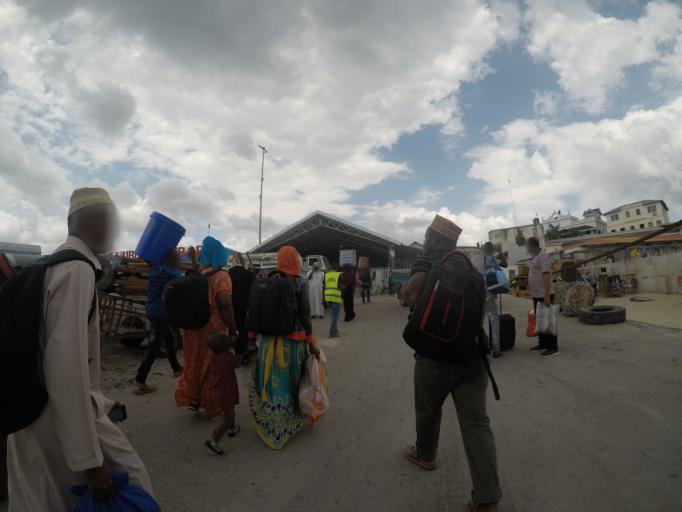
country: TZ
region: Zanzibar Urban/West
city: Zanzibar
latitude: -6.1578
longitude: 39.1919
